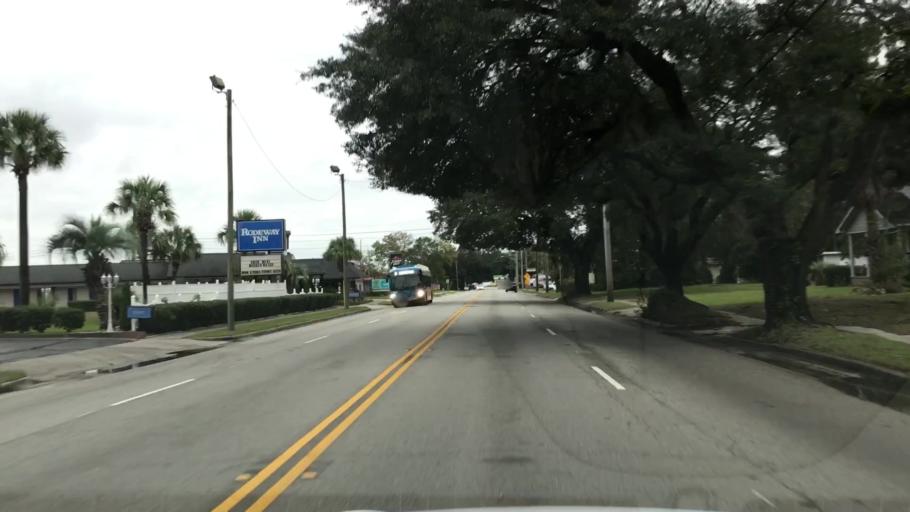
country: US
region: South Carolina
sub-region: Georgetown County
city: Georgetown
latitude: 33.3699
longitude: -79.2778
